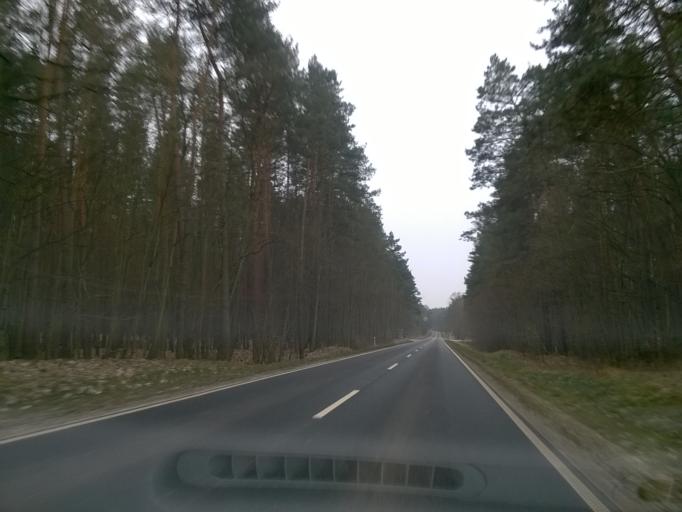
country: PL
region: Kujawsko-Pomorskie
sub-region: Powiat nakielski
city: Kcynia
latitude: 53.0529
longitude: 17.5602
